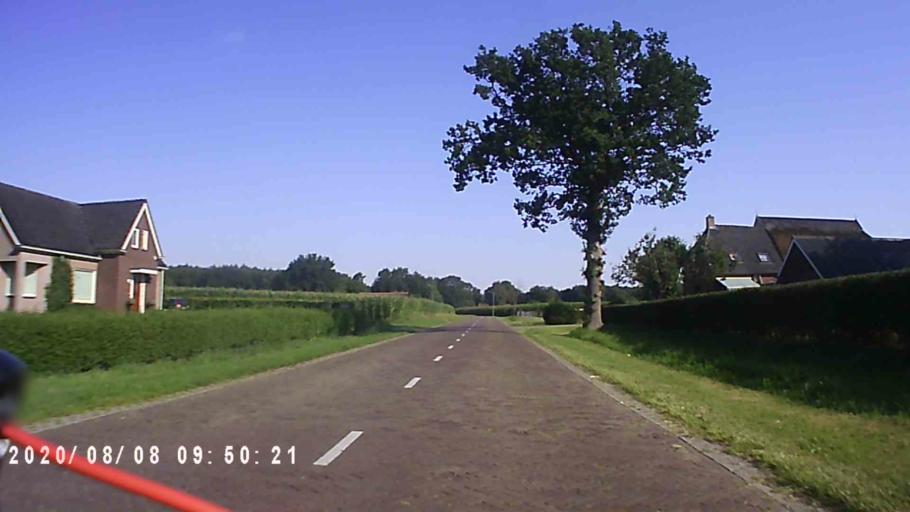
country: NL
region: Groningen
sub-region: Gemeente Leek
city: Leek
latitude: 53.0851
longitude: 6.3888
